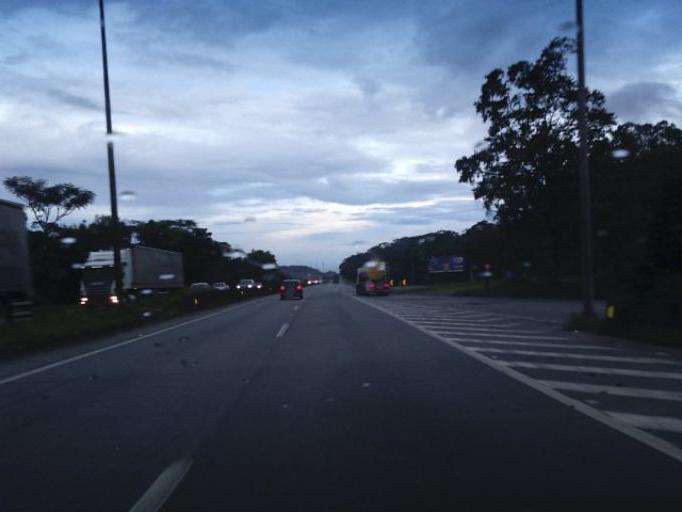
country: BR
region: Santa Catarina
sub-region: Joinville
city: Joinville
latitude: -26.0591
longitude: -48.8599
